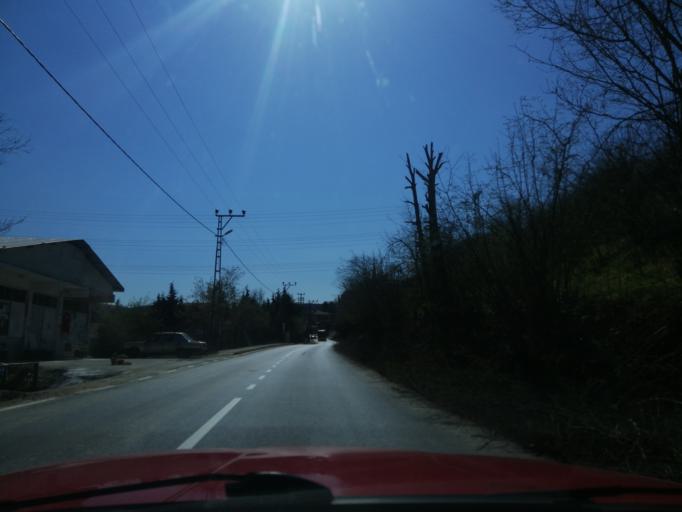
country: TR
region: Istanbul
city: Mahmut Sevket Pasa
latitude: 41.1303
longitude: 29.1620
